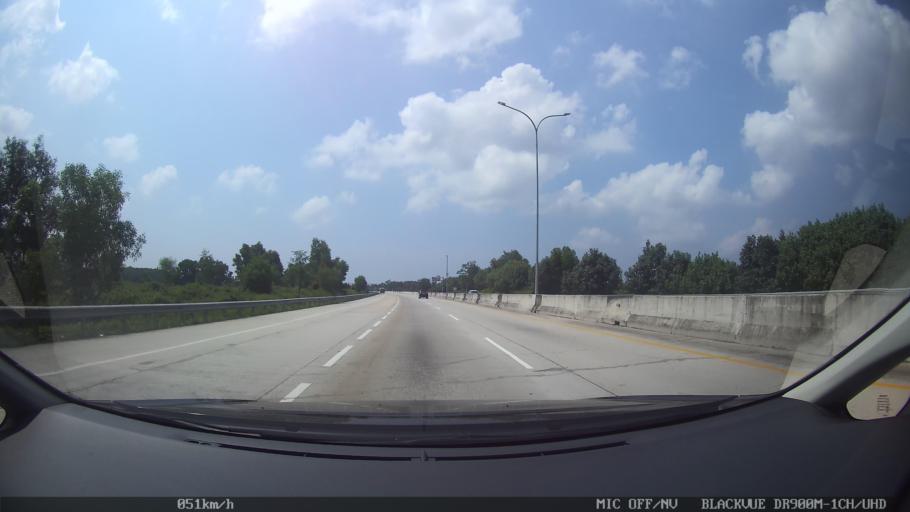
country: ID
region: Lampung
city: Natar
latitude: -5.2804
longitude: 105.2173
